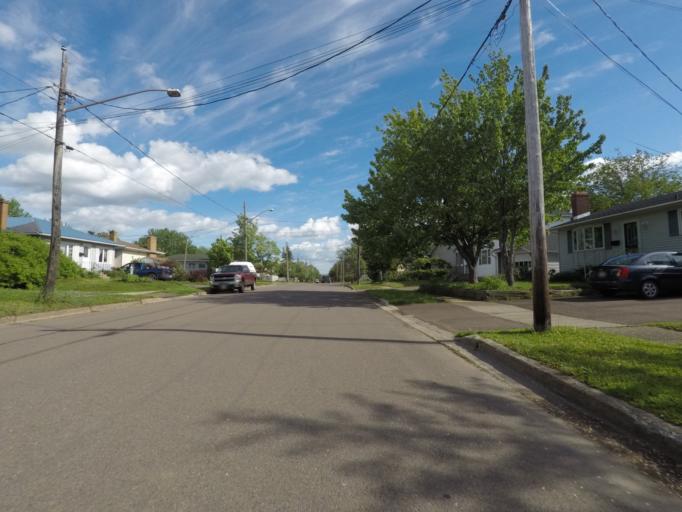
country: CA
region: New Brunswick
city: Moncton
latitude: 46.1017
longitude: -64.8227
